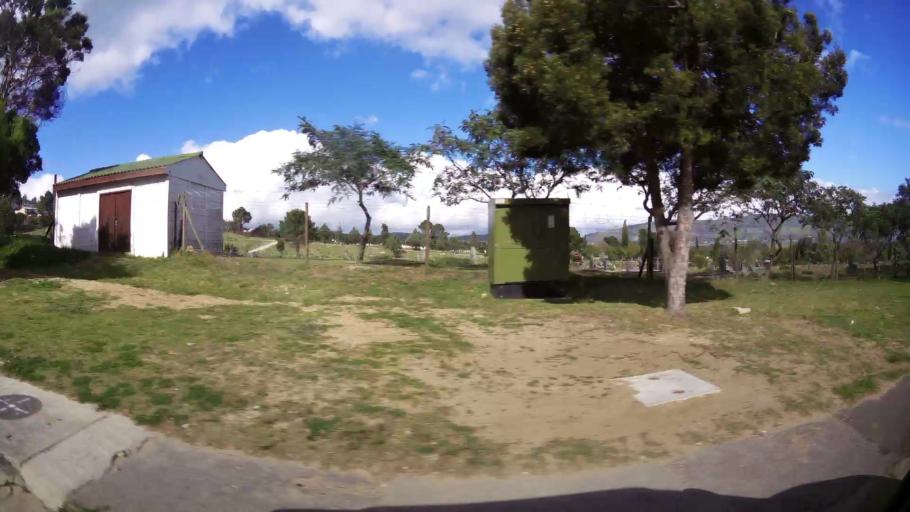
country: ZA
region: Western Cape
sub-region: Eden District Municipality
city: Knysna
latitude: -34.0477
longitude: 23.0790
